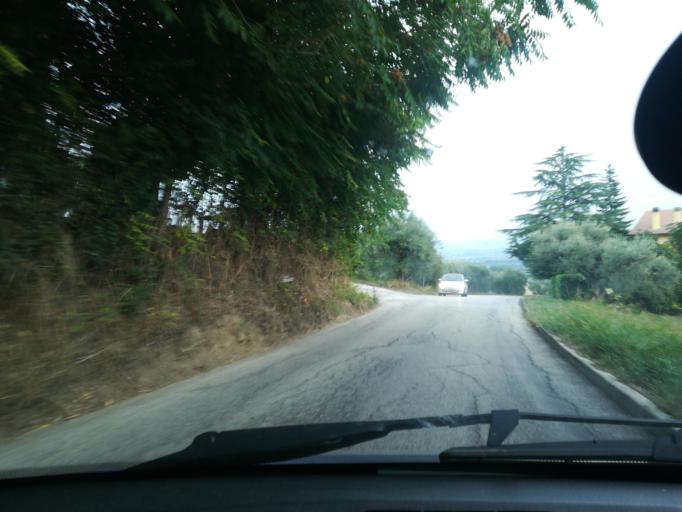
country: IT
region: The Marches
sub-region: Provincia di Macerata
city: Piediripa
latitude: 43.2942
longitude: 13.4866
